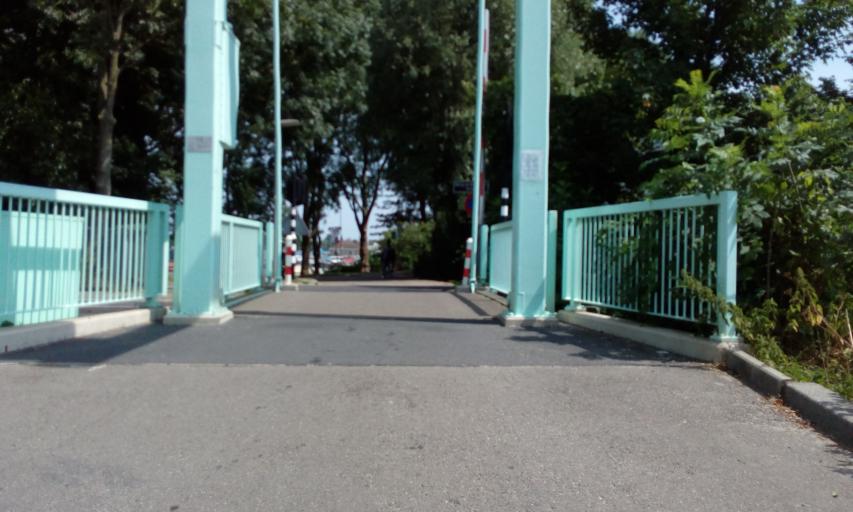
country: NL
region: South Holland
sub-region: Gemeente Rotterdam
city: Rotterdam
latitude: 51.9460
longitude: 4.4901
